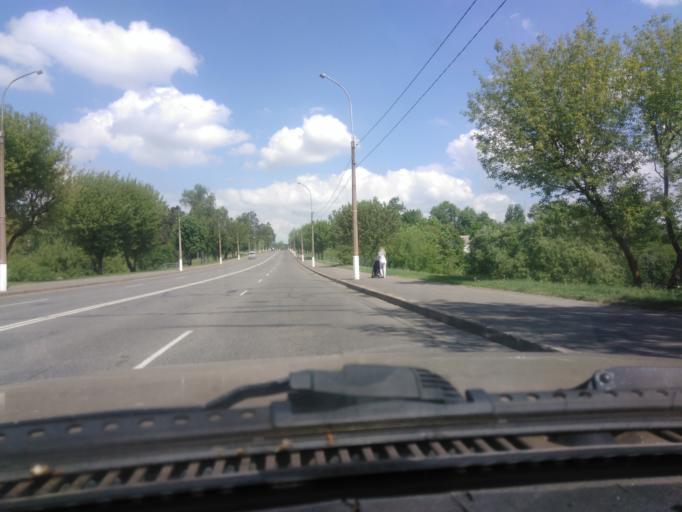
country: BY
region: Mogilev
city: Mahilyow
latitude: 53.9226
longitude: 30.3119
